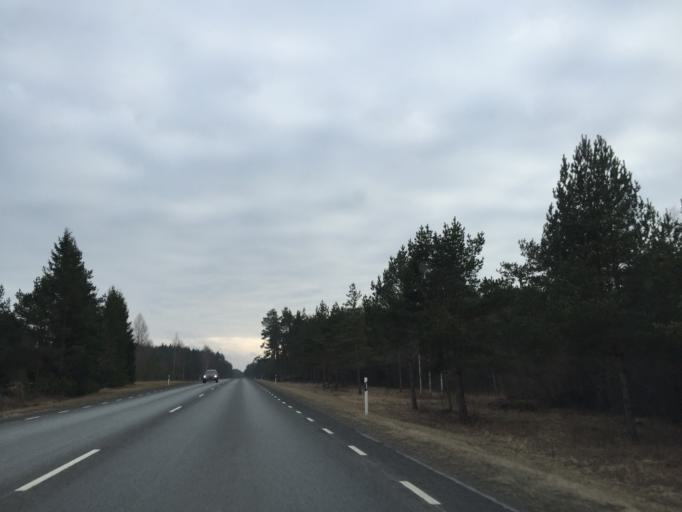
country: EE
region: Saare
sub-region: Orissaare vald
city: Orissaare
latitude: 58.5081
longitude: 22.8709
